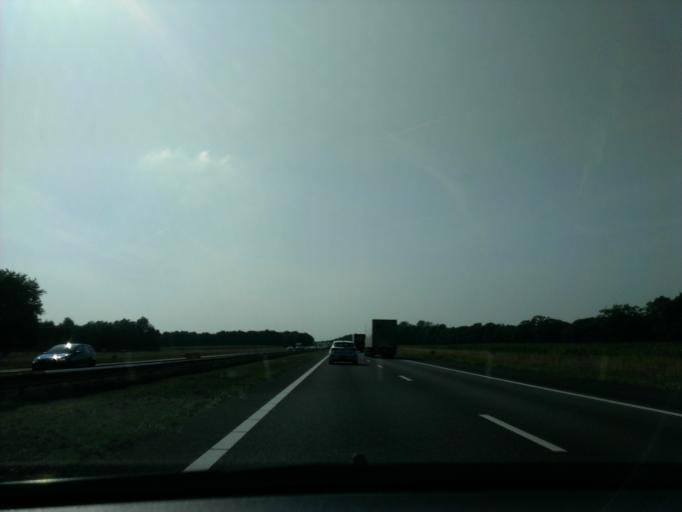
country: NL
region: Gelderland
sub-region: Gemeente Lochem
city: Harfsen
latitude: 52.2432
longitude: 6.2966
